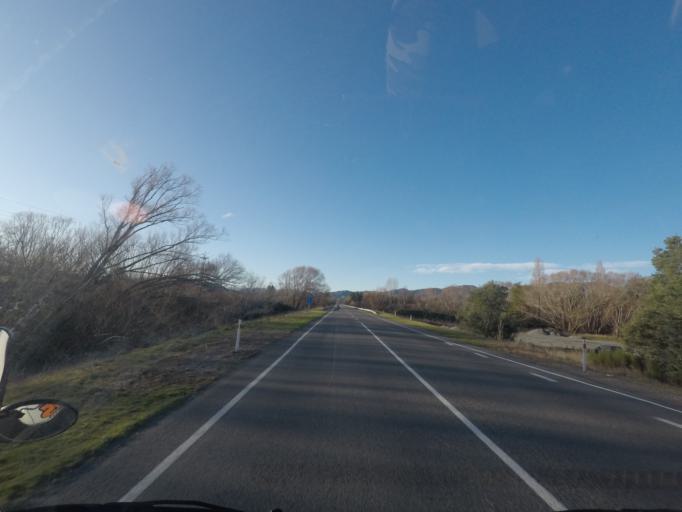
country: NZ
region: Canterbury
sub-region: Kaikoura District
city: Kaikoura
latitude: -42.7249
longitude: 173.2812
